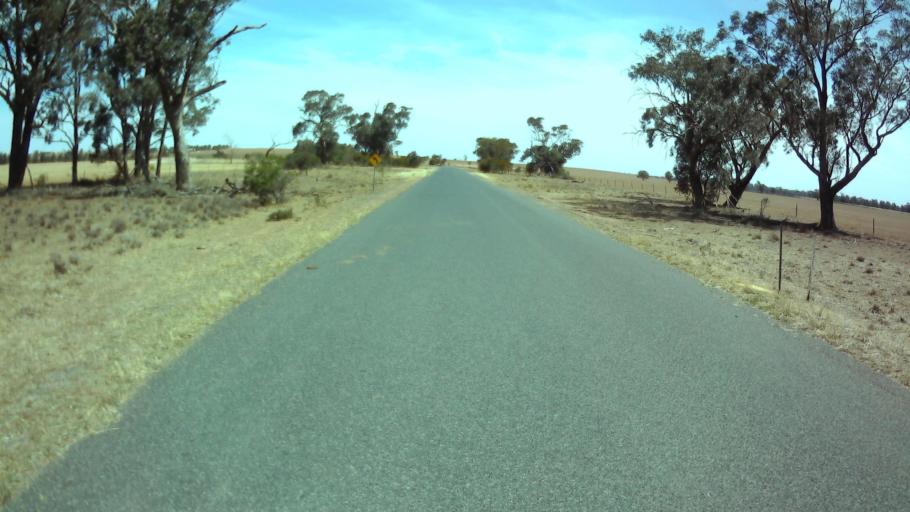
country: AU
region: New South Wales
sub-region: Weddin
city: Grenfell
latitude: -33.8846
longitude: 147.7422
